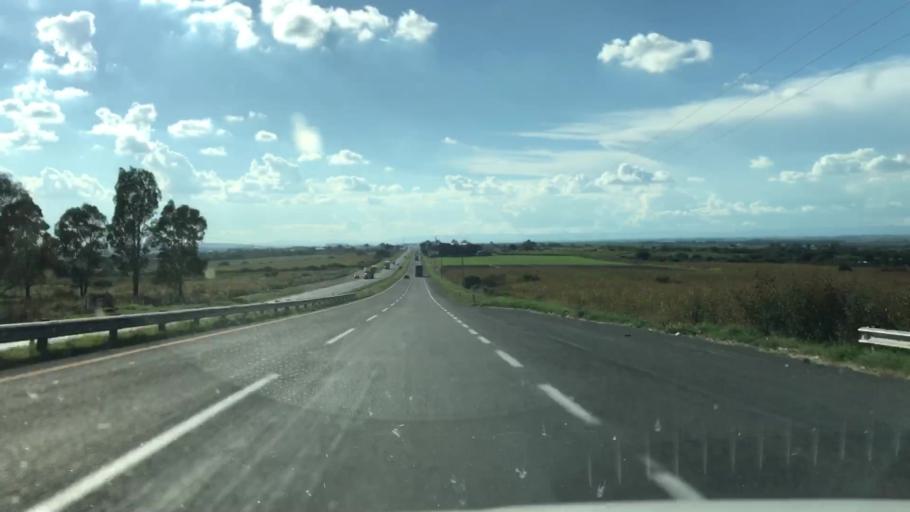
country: MX
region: Jalisco
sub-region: San Juan de los Lagos
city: Mezquitic de la Magdalena
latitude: 21.2895
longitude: -102.2219
